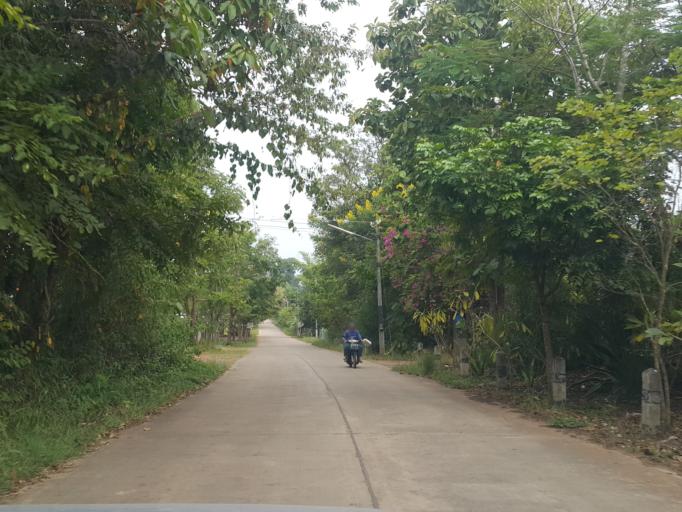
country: TH
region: Mae Hong Son
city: Wiang Nuea
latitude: 19.3693
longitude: 98.4492
